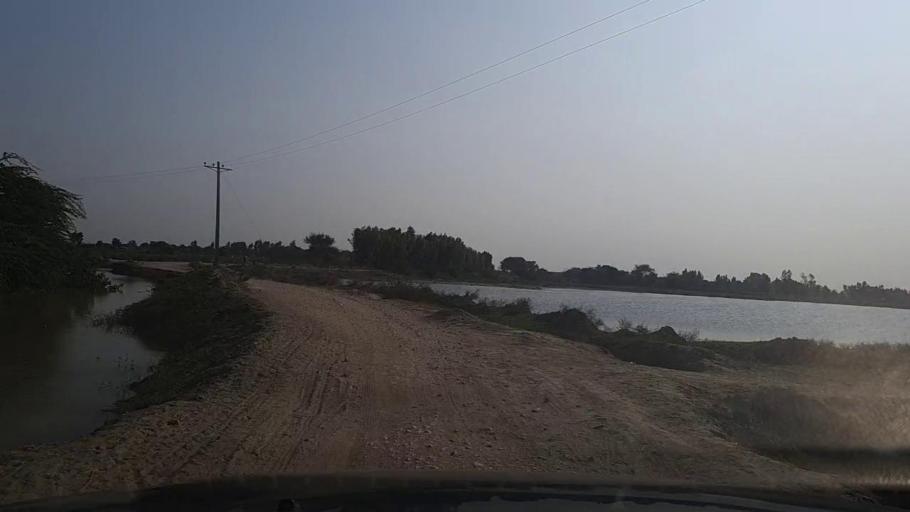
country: PK
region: Sindh
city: Mirpur Sakro
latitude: 24.6293
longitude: 67.7560
